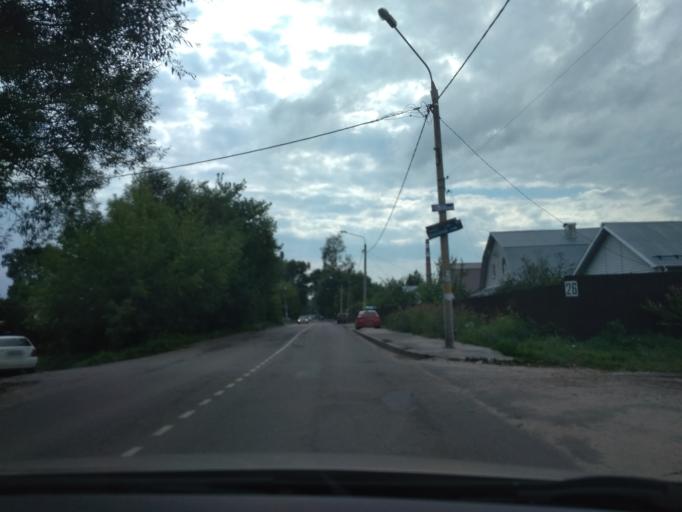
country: RU
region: Moskovskaya
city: Orekhovo-Zuyevo
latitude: 55.8018
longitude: 38.9507
